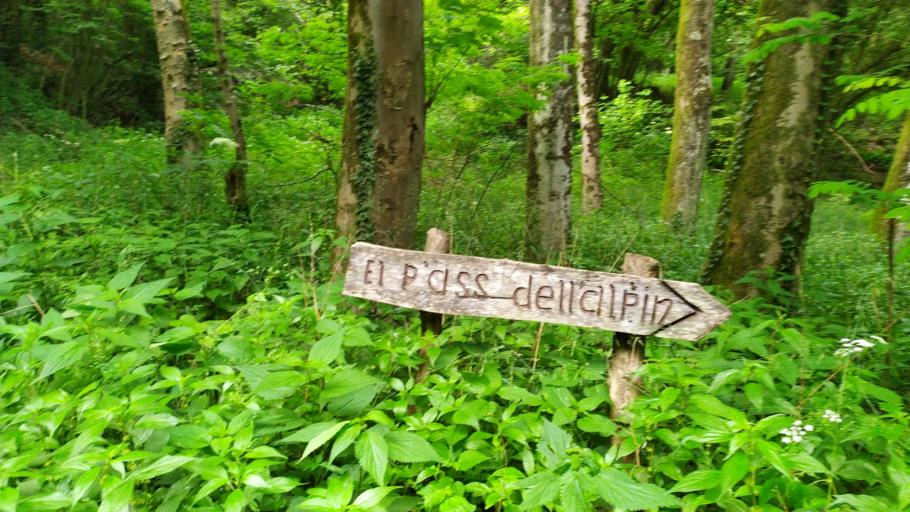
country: IT
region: Veneto
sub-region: Provincia di Vicenza
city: Torrebelvicino
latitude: 45.6880
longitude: 11.3148
